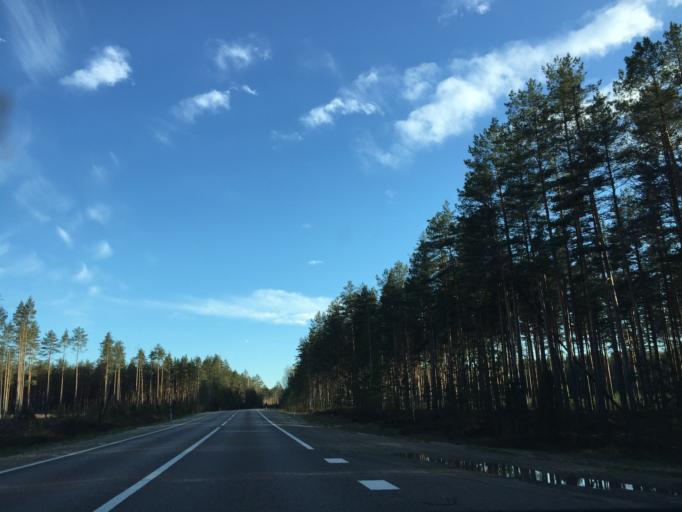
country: LV
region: Strenci
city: Seda
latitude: 57.6626
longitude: 25.8735
